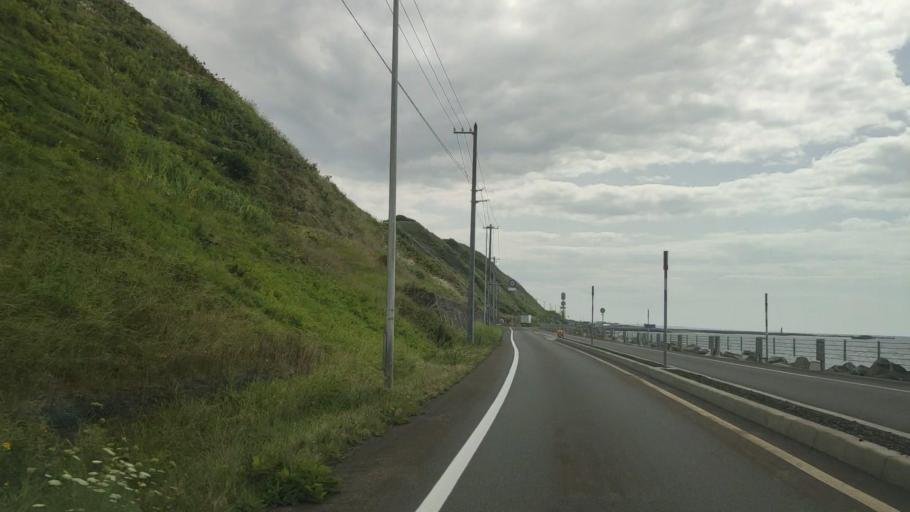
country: JP
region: Hokkaido
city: Rumoi
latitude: 44.5449
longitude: 141.7669
